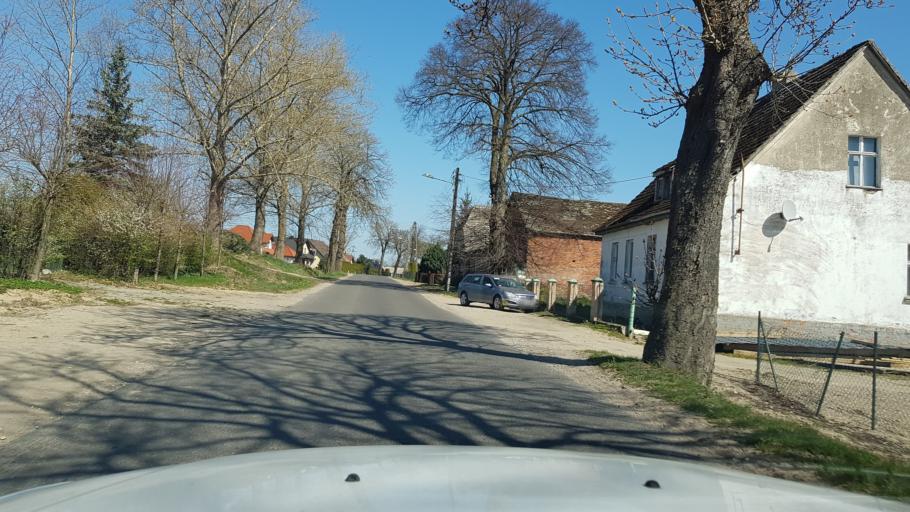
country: PL
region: West Pomeranian Voivodeship
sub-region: Powiat slawienski
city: Slawno
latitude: 54.3866
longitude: 16.6991
